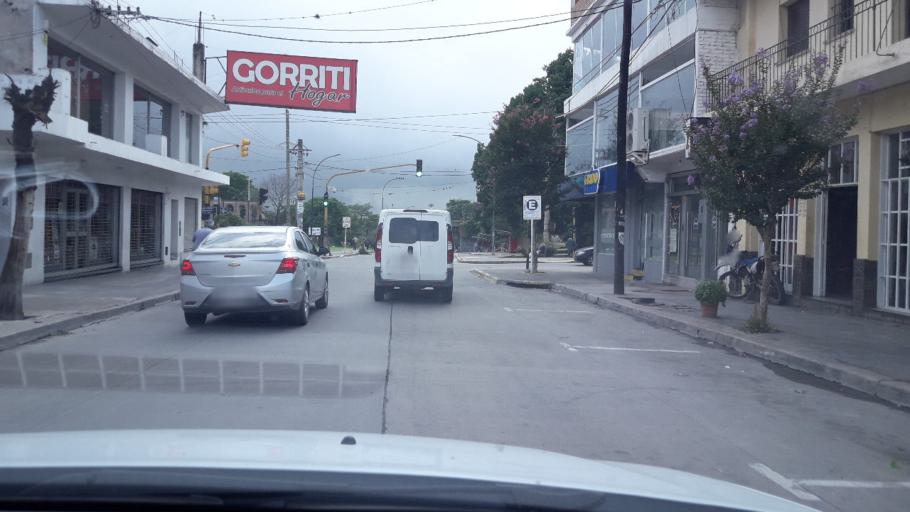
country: AR
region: Jujuy
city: San Salvador de Jujuy
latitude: -24.1919
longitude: -65.2949
